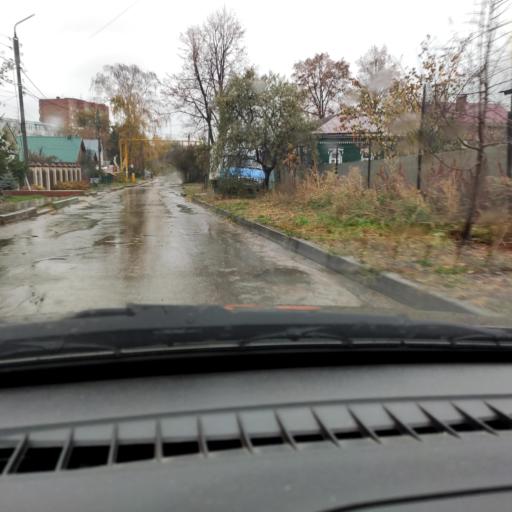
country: RU
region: Samara
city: Tol'yatti
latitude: 53.5277
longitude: 49.4047
